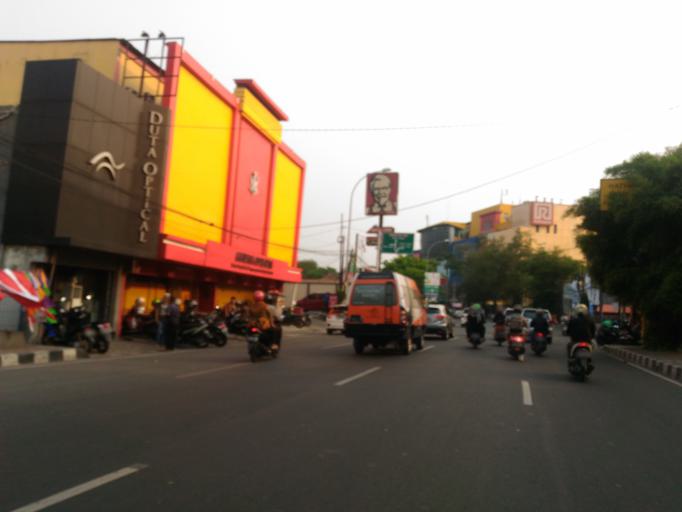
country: ID
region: Banten
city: Tangerang
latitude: -6.1731
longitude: 106.6307
